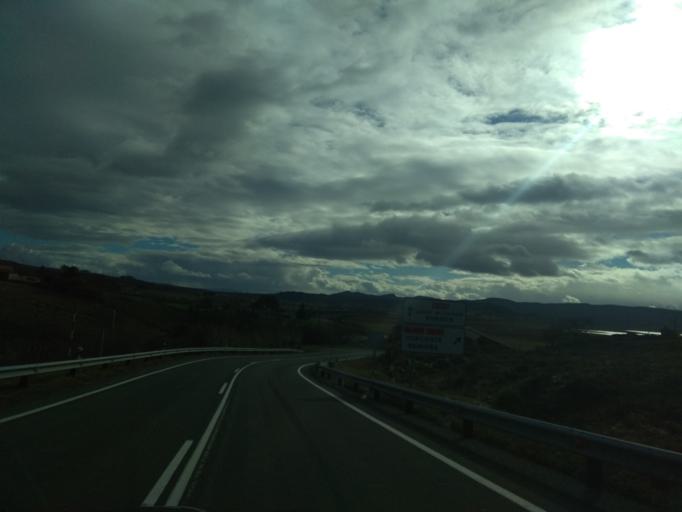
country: ES
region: Castille and Leon
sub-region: Provincia de Burgos
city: Arija
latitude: 43.0306
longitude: -3.8639
